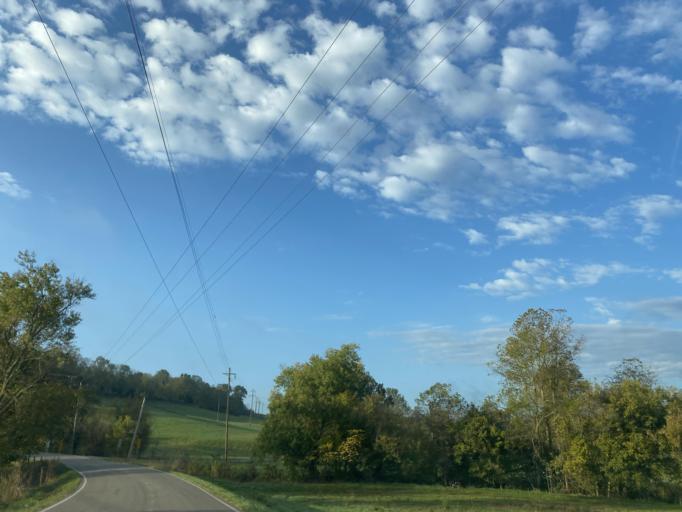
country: US
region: Kentucky
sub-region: Pendleton County
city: Falmouth
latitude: 38.7717
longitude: -84.3381
